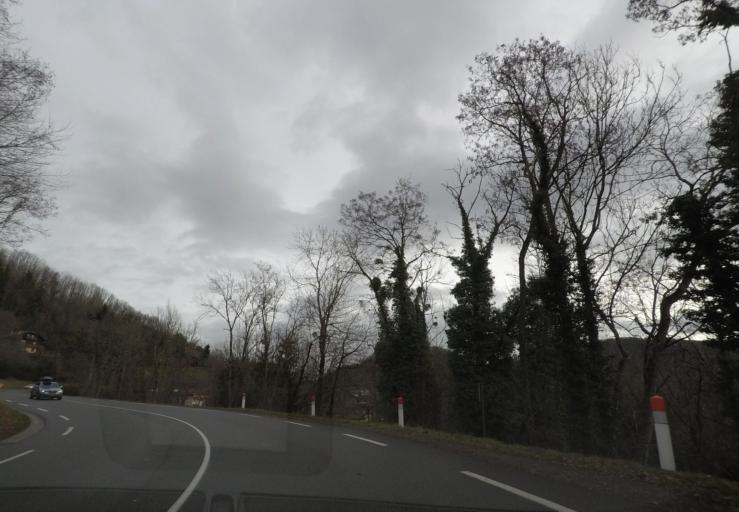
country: FR
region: Rhone-Alpes
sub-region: Departement de la Haute-Savoie
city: Chatillon-sur-Cluses
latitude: 46.0839
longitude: 6.5750
